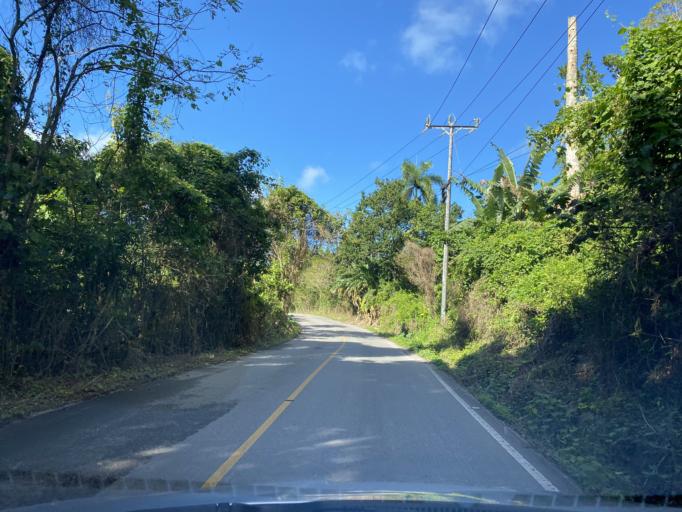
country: DO
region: Samana
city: Sanchez
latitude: 19.2424
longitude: -69.5952
